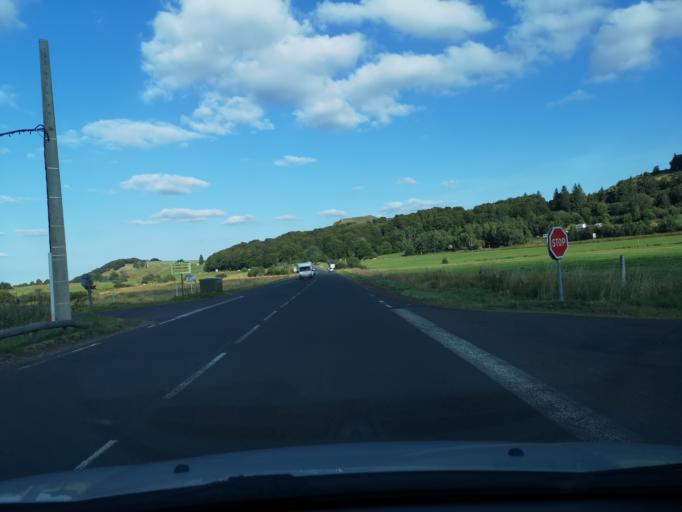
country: FR
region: Auvergne
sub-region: Departement du Puy-de-Dome
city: Mont-Dore
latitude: 45.5036
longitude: 2.8852
